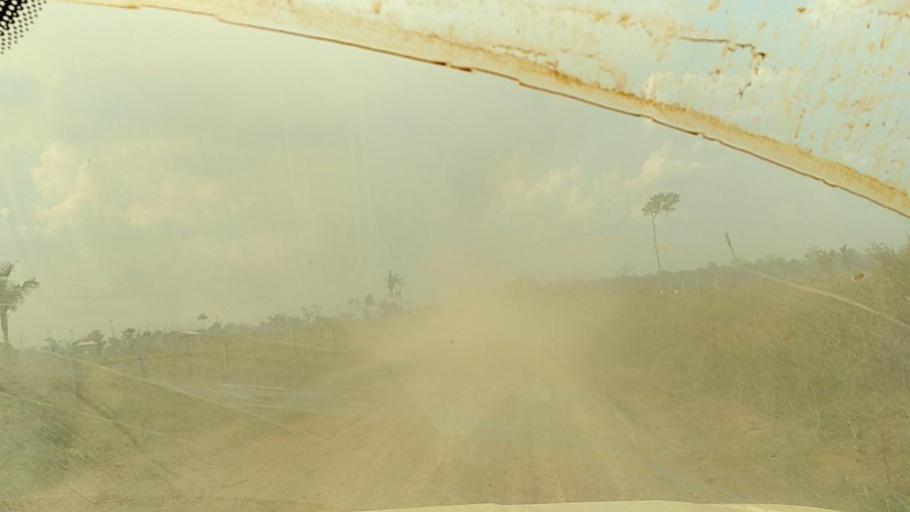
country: BR
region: Rondonia
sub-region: Porto Velho
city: Porto Velho
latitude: -8.6872
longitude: -63.2392
